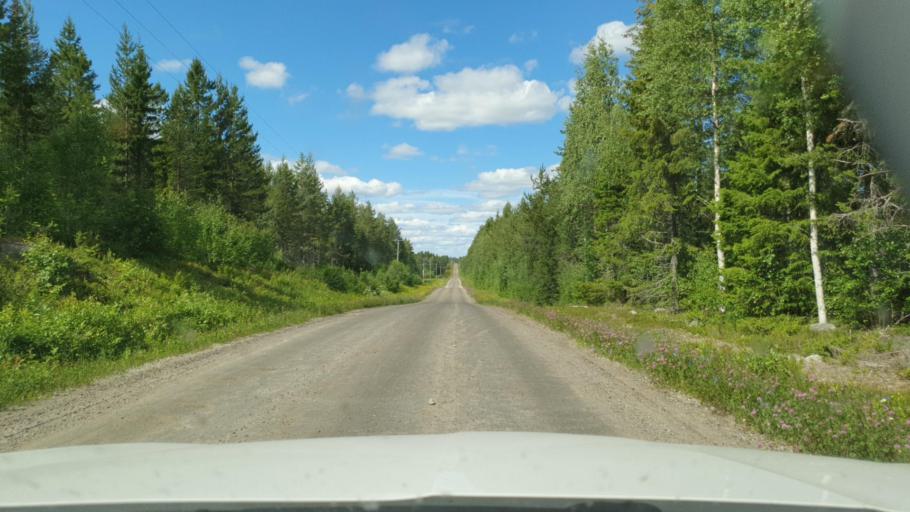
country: SE
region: Vaesterbotten
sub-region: Skelleftea Kommun
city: Backa
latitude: 65.1690
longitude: 21.1176
